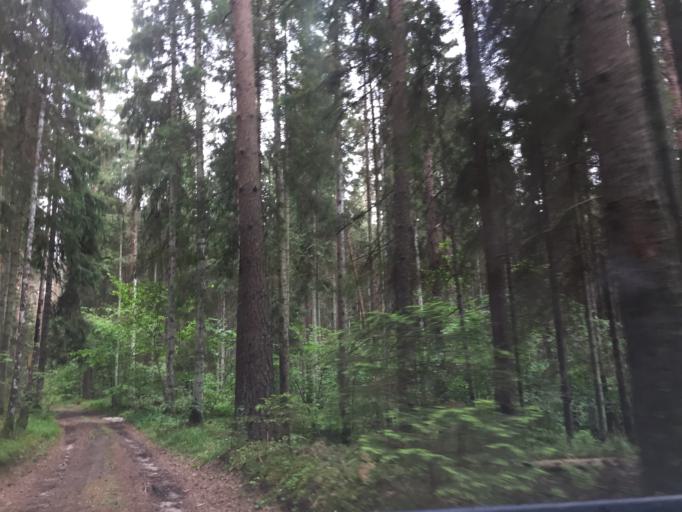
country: LV
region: Tukuma Rajons
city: Tukums
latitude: 57.0242
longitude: 23.0758
